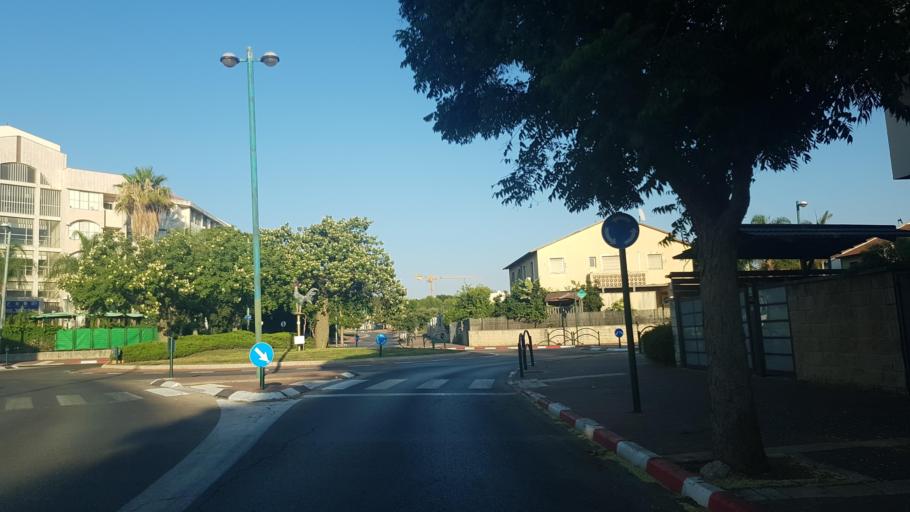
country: IL
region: Central District
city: Kfar Saba
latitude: 32.1816
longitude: 34.9348
